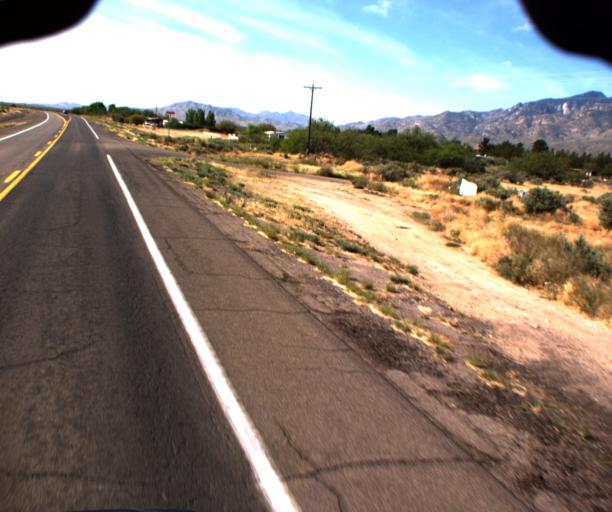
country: US
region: Arizona
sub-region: Graham County
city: Swift Trail Junction
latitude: 32.6897
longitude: -109.7077
